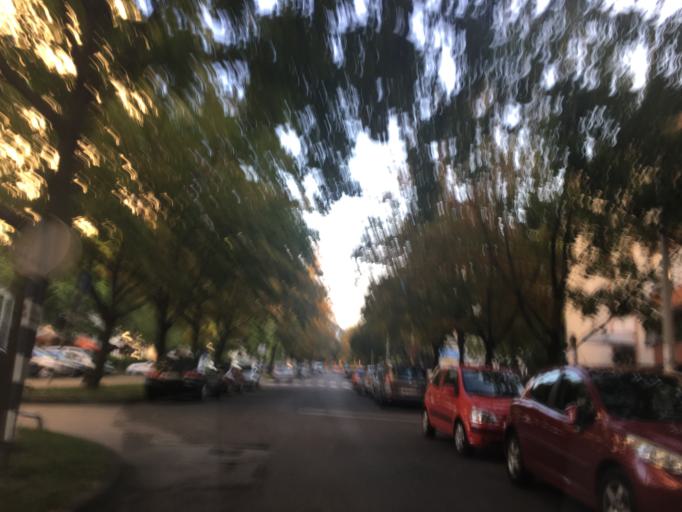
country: HR
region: Grad Zagreb
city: Jankomir
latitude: 45.7897
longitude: 15.9385
